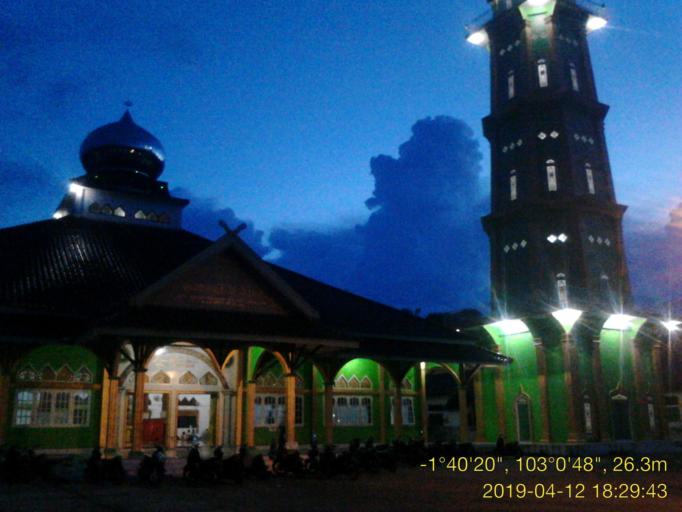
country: ID
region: Jambi
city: Mersam
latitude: -1.6723
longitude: 103.0135
